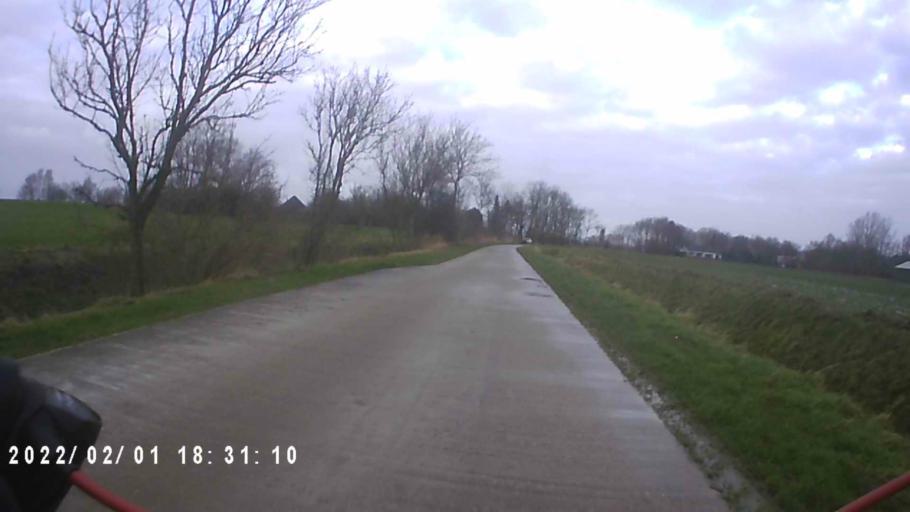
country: NL
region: Groningen
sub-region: Gemeente De Marne
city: Ulrum
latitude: 53.3576
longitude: 6.3200
